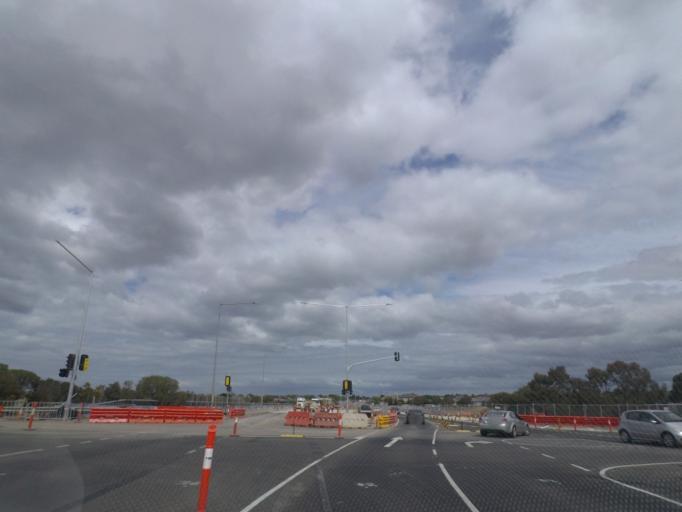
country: AU
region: Victoria
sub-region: Wyndham
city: Williams Landing
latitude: -37.8734
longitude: 144.7491
